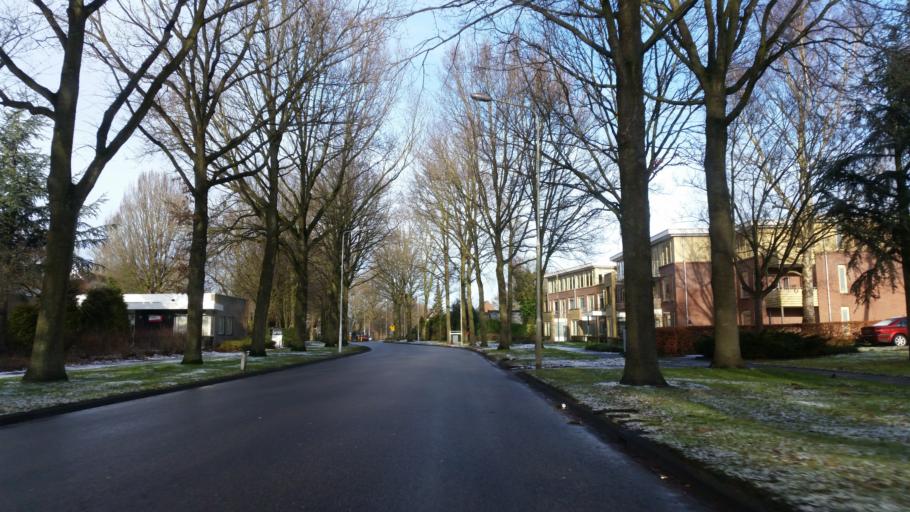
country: NL
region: Friesland
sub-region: Gemeente Tytsjerksteradiel
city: Burgum
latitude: 53.1927
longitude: 5.9974
